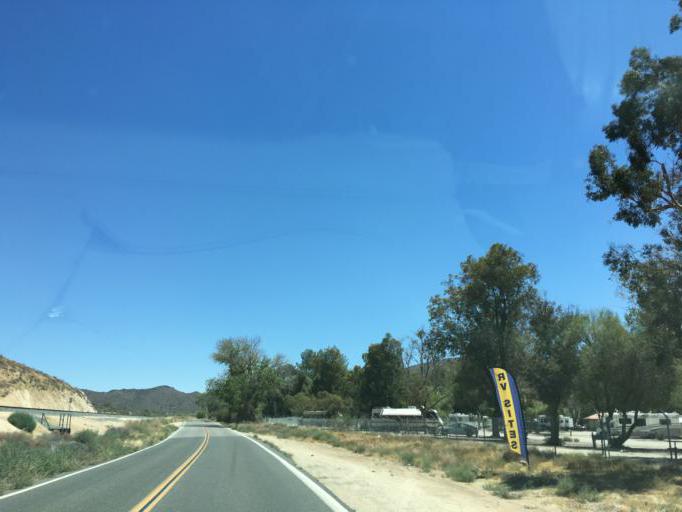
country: US
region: California
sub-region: Los Angeles County
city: Acton
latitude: 34.4482
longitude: -118.2066
